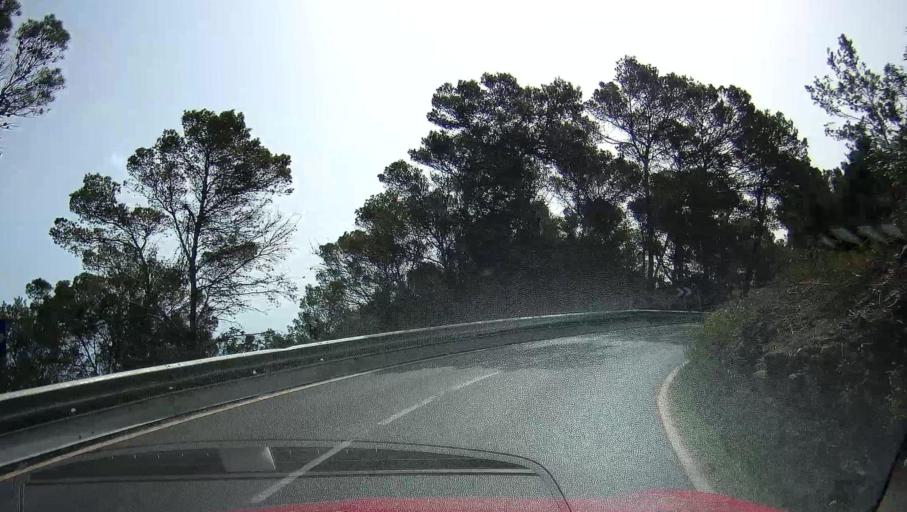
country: ES
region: Balearic Islands
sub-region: Illes Balears
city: Sant Joan de Labritja
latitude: 39.0624
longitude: 1.5844
